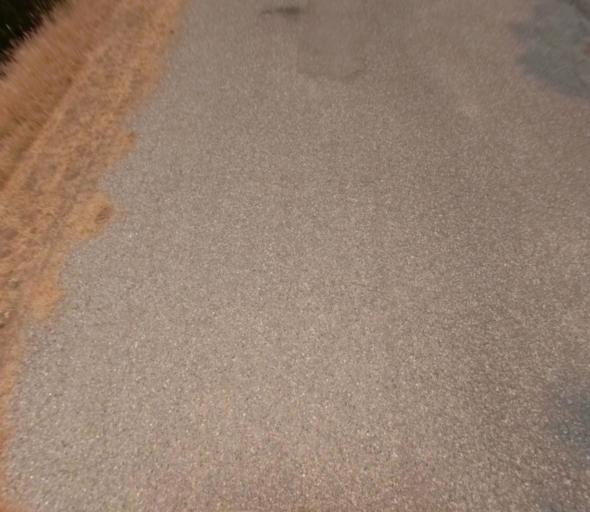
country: US
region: California
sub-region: Madera County
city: Oakhurst
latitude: 37.3329
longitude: -119.6044
